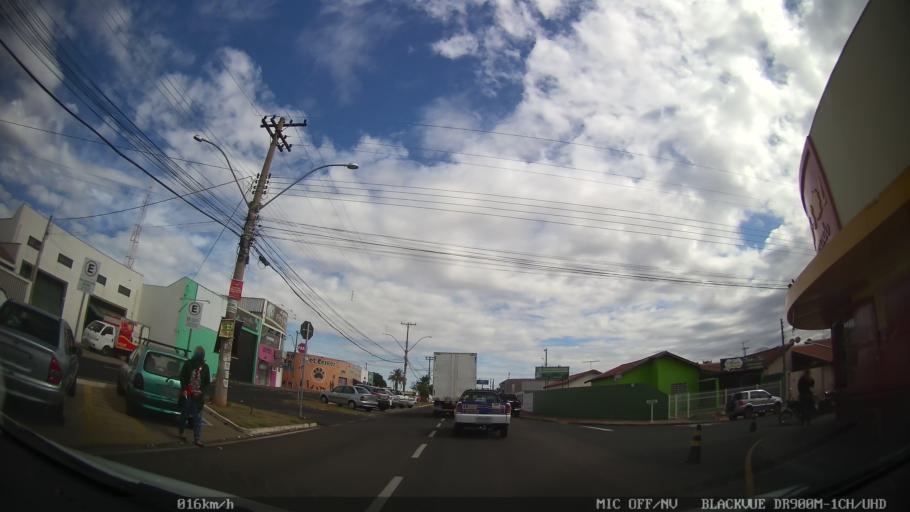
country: BR
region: Sao Paulo
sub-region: Sao Jose Do Rio Preto
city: Sao Jose do Rio Preto
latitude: -20.8043
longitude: -49.4960
